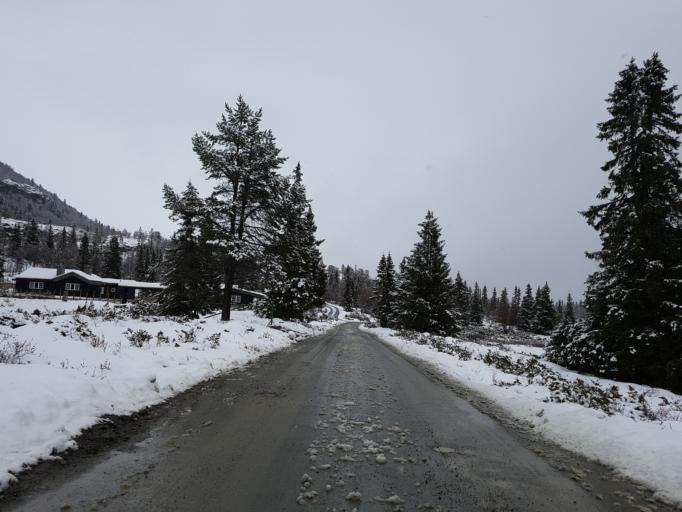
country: NO
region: Oppland
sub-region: Sel
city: Otta
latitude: 61.8047
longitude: 9.6954
